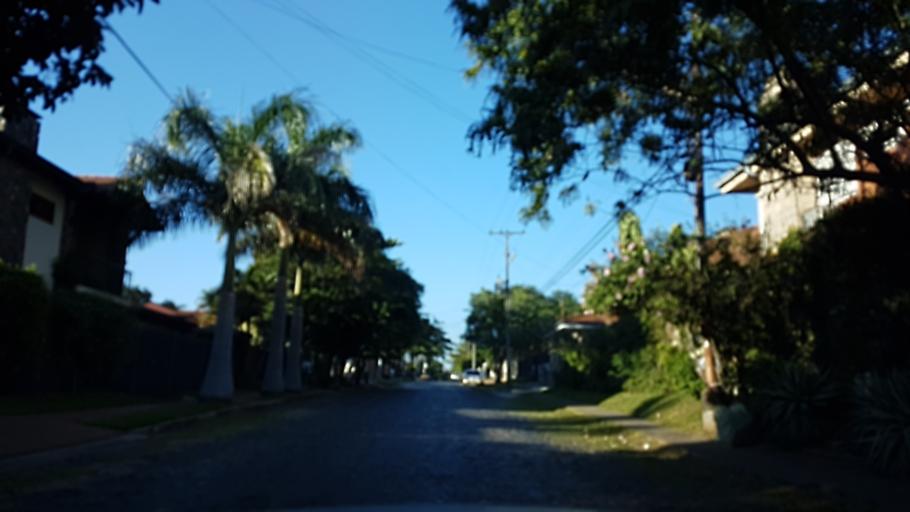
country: PY
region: Central
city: Fernando de la Mora
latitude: -25.2663
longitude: -57.5552
